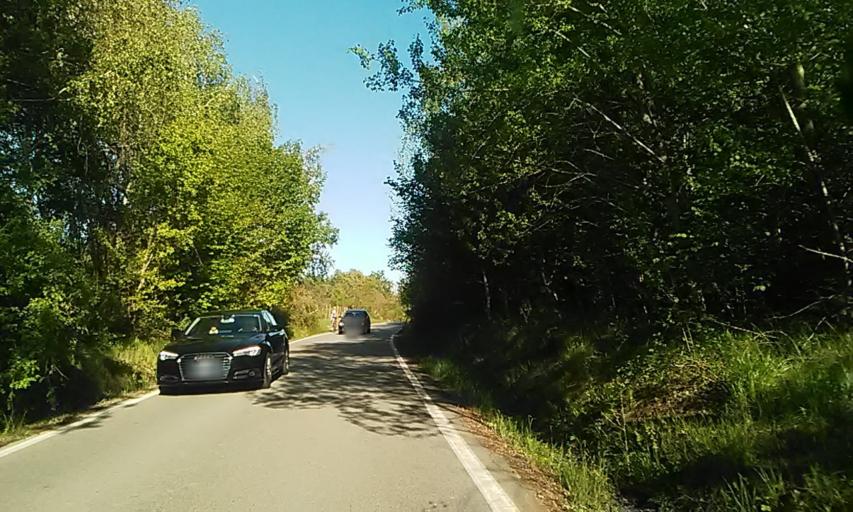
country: IT
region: Piedmont
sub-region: Provincia di Novara
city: Cavaglio D'Agogna
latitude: 45.6155
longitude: 8.4614
